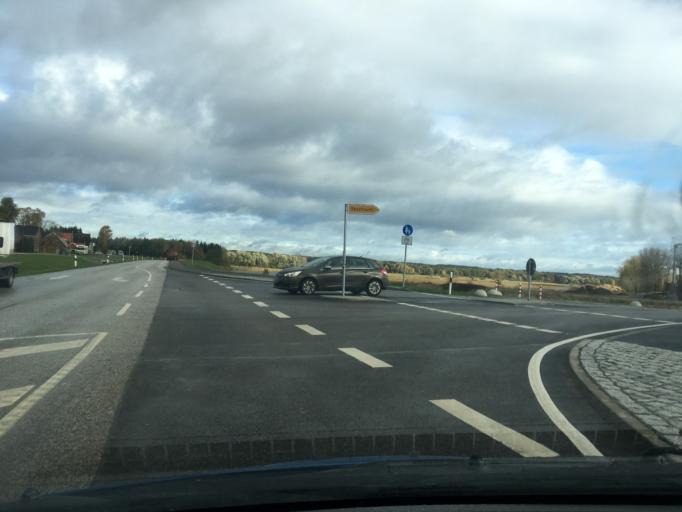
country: DE
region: Schleswig-Holstein
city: Escheburg
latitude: 53.4344
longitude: 10.3002
